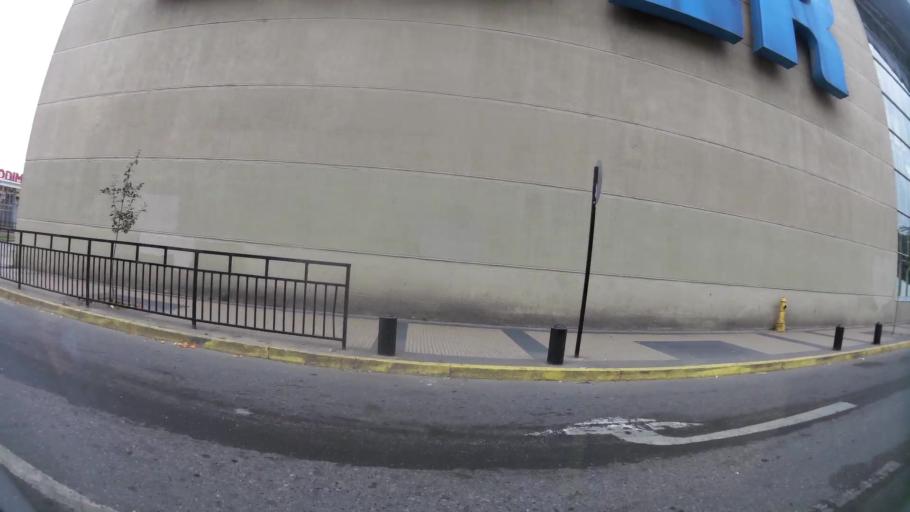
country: CL
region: Biobio
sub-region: Provincia de Concepcion
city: Concepcion
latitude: -36.8295
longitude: -73.0608
